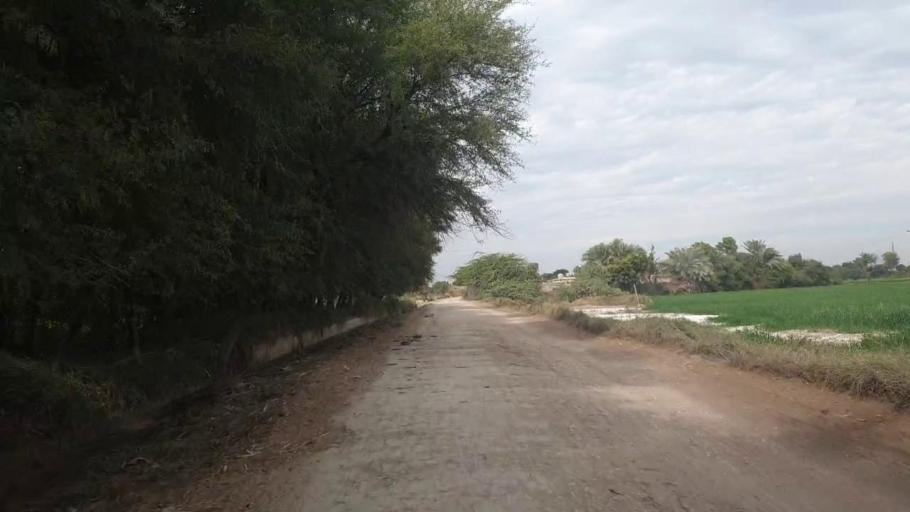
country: PK
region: Sindh
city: Sinjhoro
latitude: 26.0244
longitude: 68.8741
